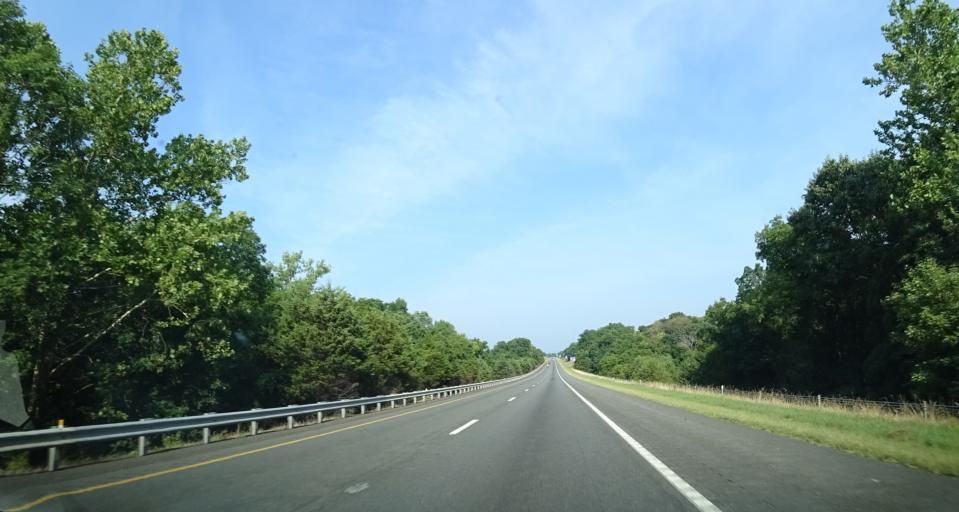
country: US
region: Virginia
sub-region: Warren County
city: Front Royal
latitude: 38.9486
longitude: -78.1596
